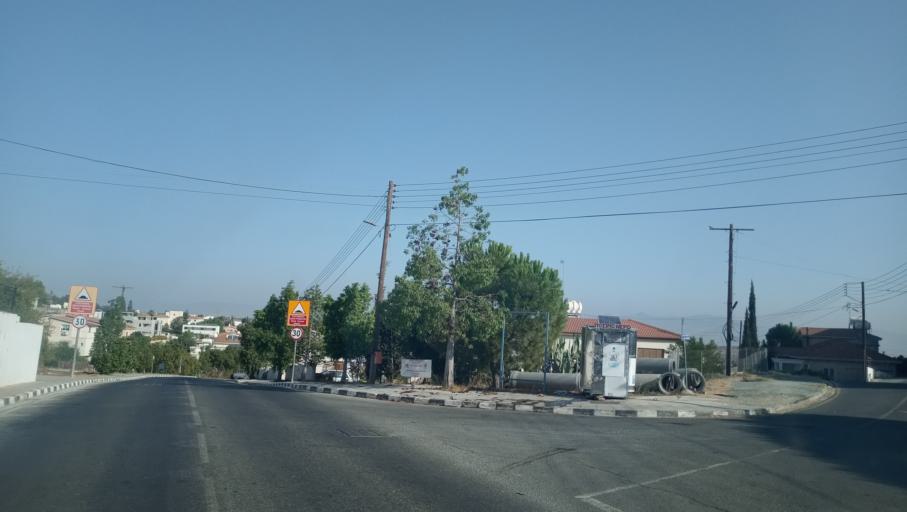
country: CY
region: Lefkosia
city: Geri
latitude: 35.1113
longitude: 33.4226
